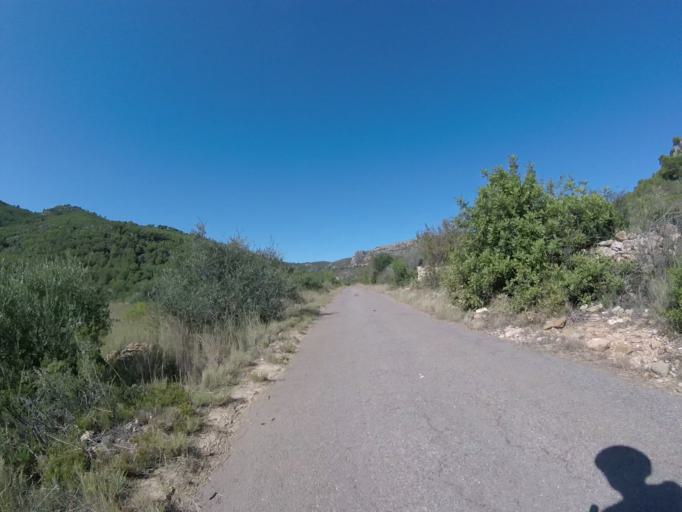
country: ES
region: Valencia
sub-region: Provincia de Castello
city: Orpesa/Oropesa del Mar
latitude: 40.1368
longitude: 0.1044
